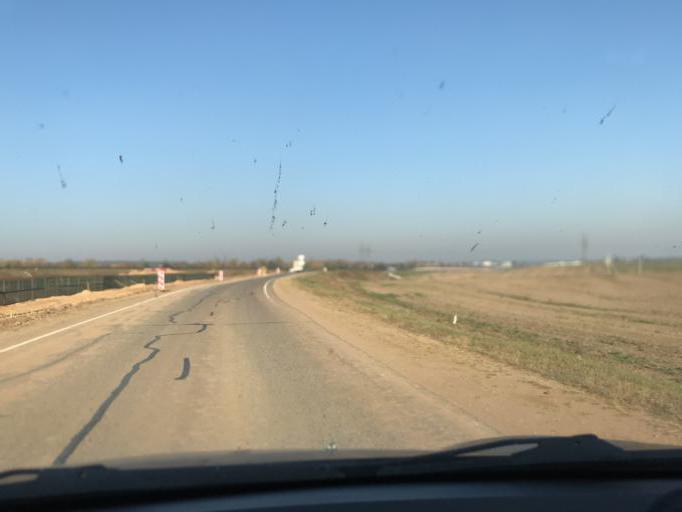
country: BY
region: Minsk
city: Pryvol'ny
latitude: 53.8043
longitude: 27.7985
